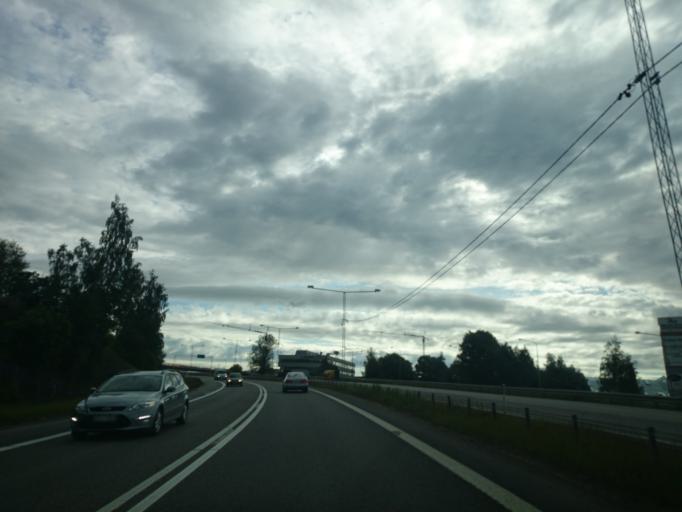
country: SE
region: Vaesternorrland
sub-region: Sundsvalls Kommun
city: Sundsvall
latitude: 62.3953
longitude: 17.3310
